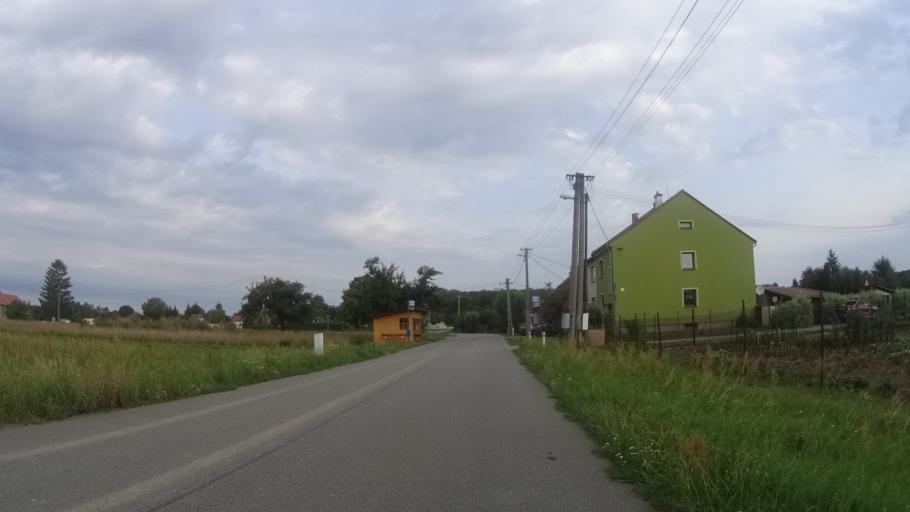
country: CZ
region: Zlin
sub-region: Okres Kromeriz
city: Kromeriz
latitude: 49.3154
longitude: 17.3893
